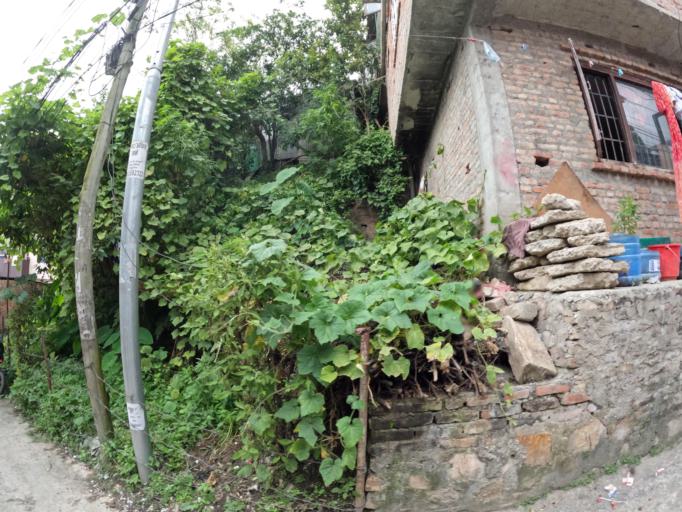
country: NP
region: Central Region
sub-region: Bagmati Zone
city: Kathmandu
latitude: 27.7389
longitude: 85.3189
